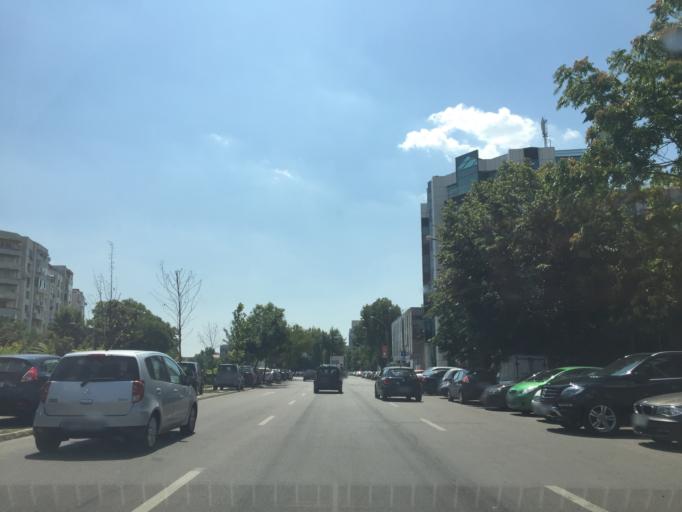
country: RO
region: Bucuresti
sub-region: Municipiul Bucuresti
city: Bucharest
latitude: 44.4203
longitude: 26.1104
